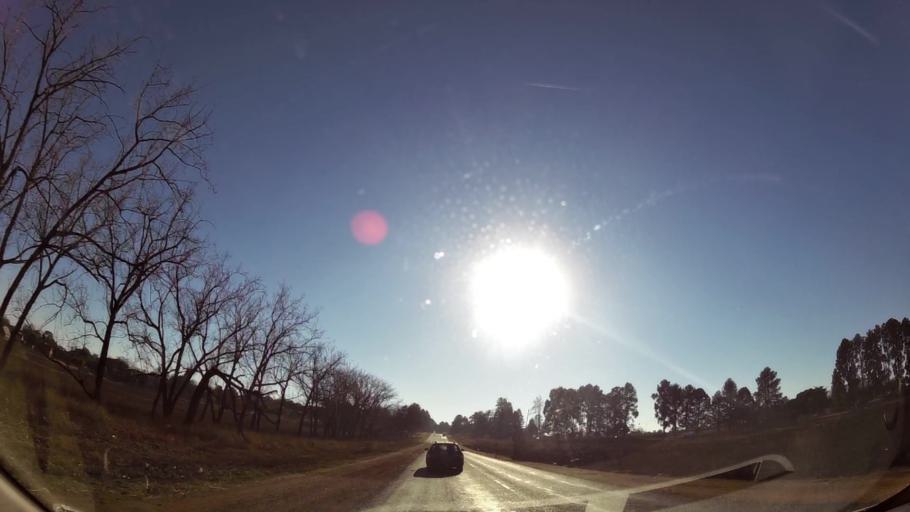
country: ZA
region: Gauteng
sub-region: Ekurhuleni Metropolitan Municipality
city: Tembisa
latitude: -26.0442
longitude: 28.2454
